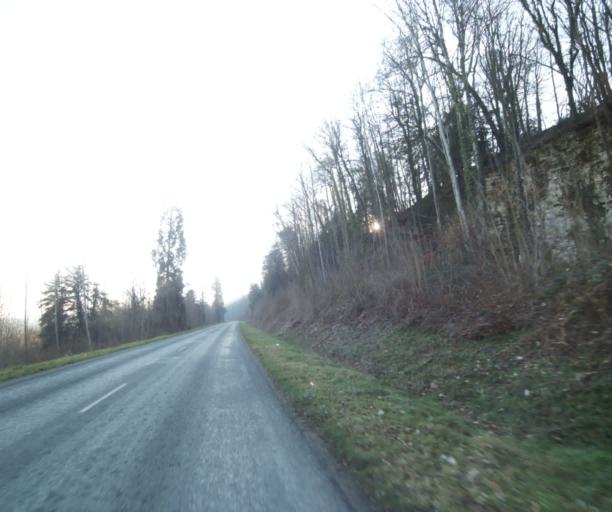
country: FR
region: Champagne-Ardenne
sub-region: Departement de la Haute-Marne
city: Bienville
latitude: 48.5778
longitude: 5.0392
